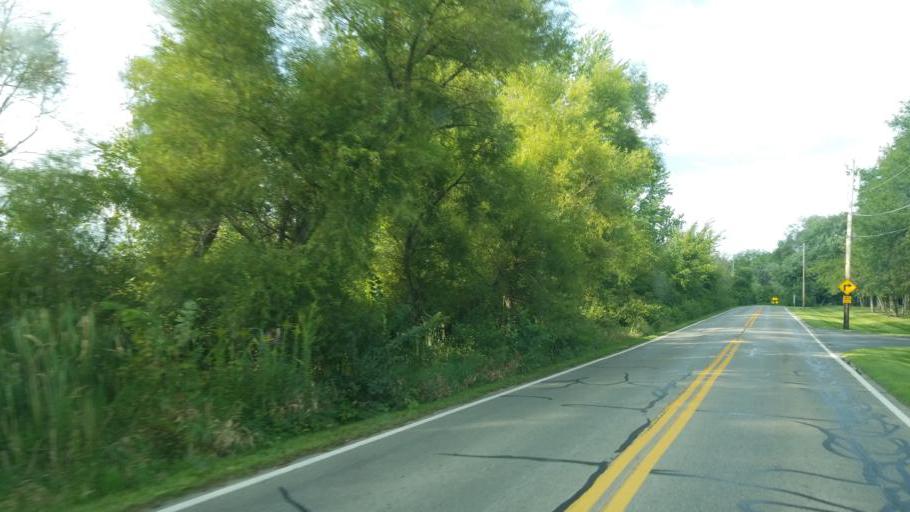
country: US
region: Ohio
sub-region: Franklin County
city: Worthington
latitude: 40.0809
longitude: -83.0549
